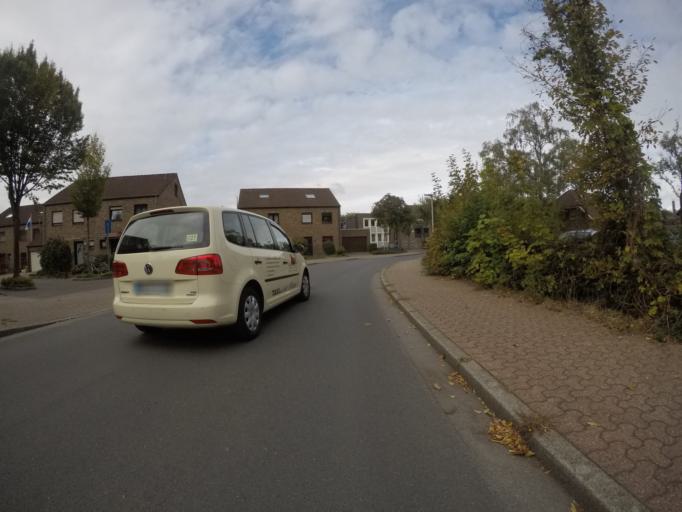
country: DE
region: North Rhine-Westphalia
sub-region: Regierungsbezirk Dusseldorf
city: Bocholt
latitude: 51.8404
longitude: 6.6275
